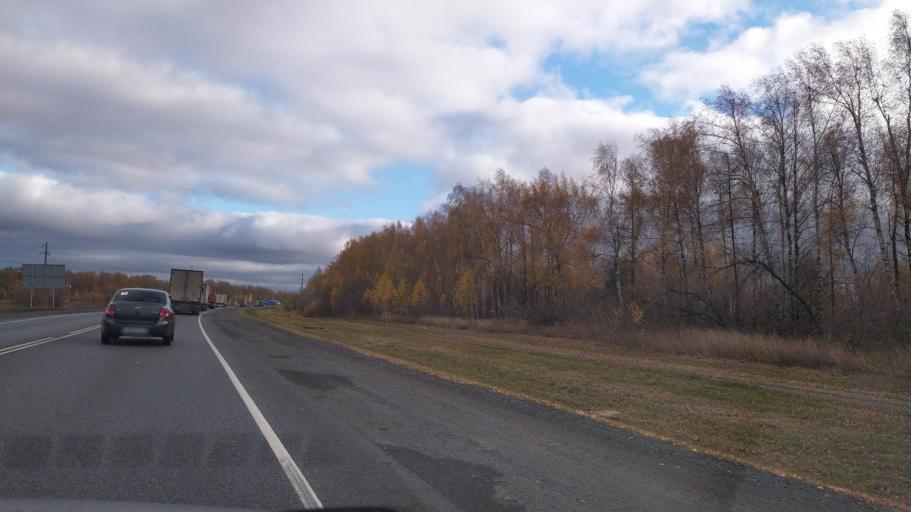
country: RU
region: Chuvashia
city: Kugesi
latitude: 56.0531
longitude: 47.2772
